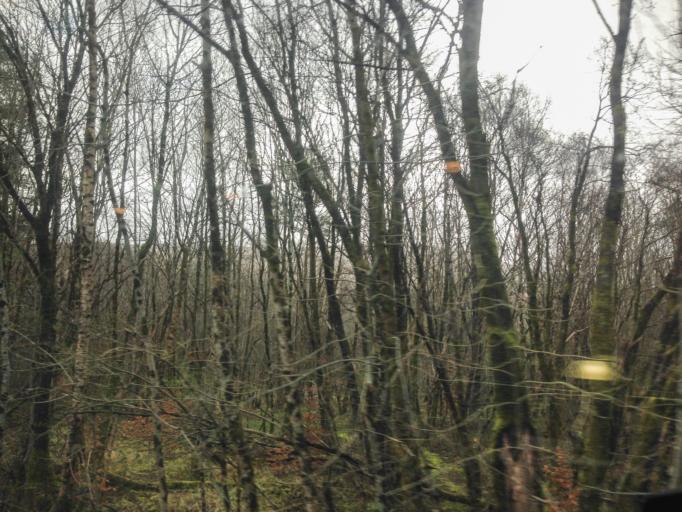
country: GB
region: Scotland
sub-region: Highland
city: Fort William
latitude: 56.8439
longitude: -5.1520
